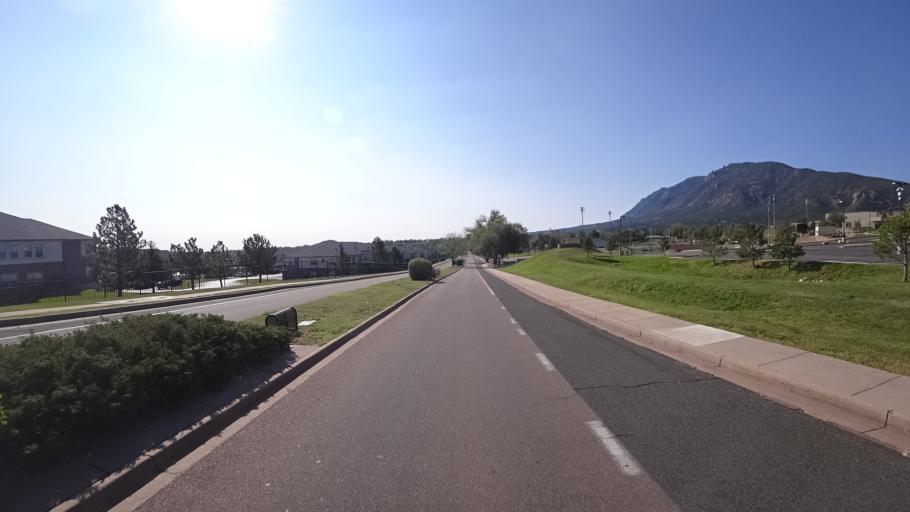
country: US
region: Colorado
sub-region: El Paso County
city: Colorado Springs
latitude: 38.8050
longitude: -104.8559
